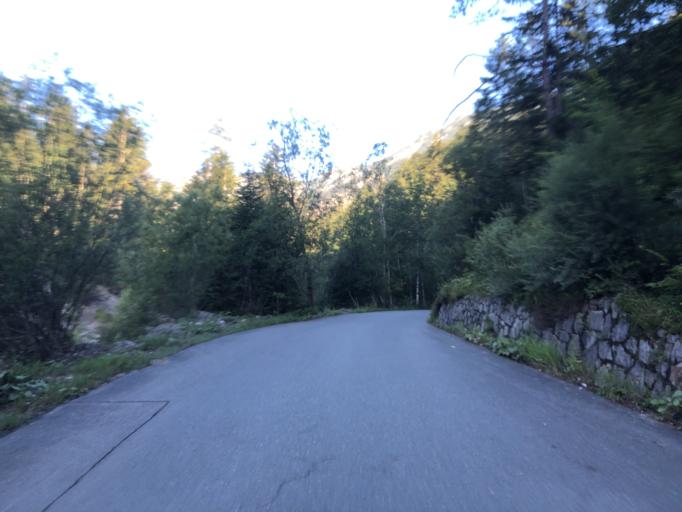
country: AT
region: Tyrol
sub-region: Politischer Bezirk Kitzbuhel
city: Schwendt
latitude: 47.5826
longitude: 12.3560
